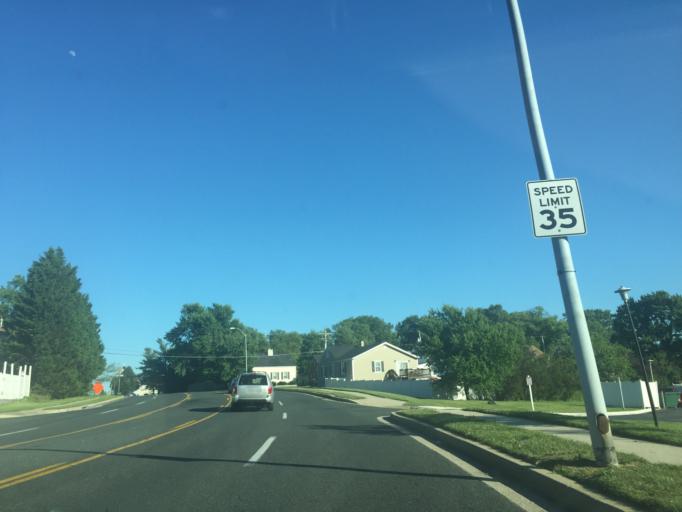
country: US
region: Maryland
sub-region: Baltimore County
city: Overlea
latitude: 39.3765
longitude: -76.5145
